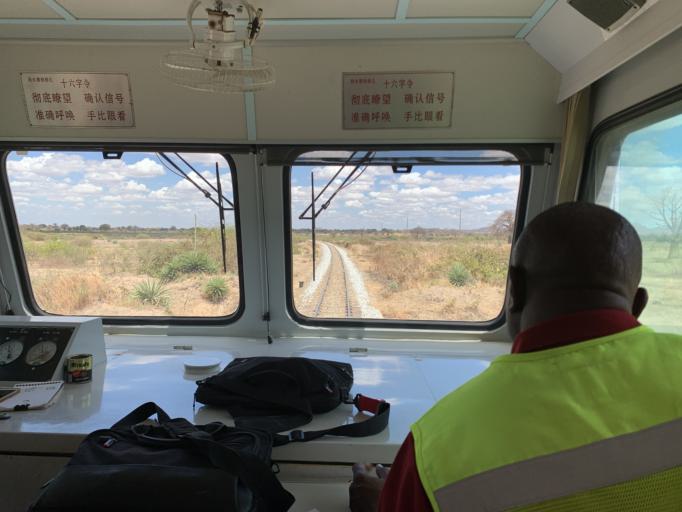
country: TZ
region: Dodoma
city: Dodoma
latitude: -6.1171
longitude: 35.5084
